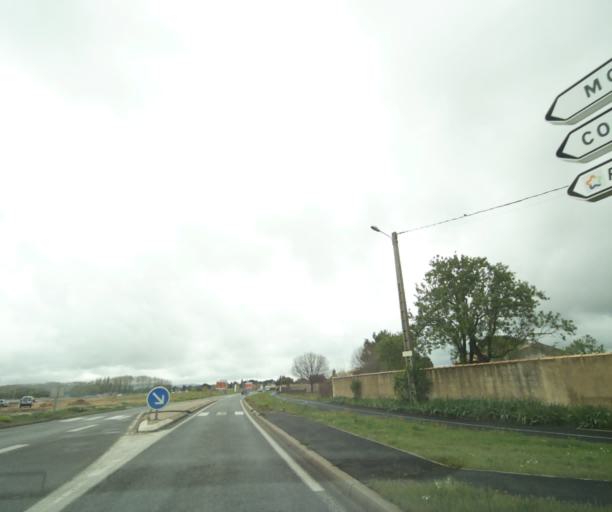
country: FR
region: Languedoc-Roussillon
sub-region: Departement de l'Herault
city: Cournonterral
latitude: 43.5574
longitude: 3.7287
